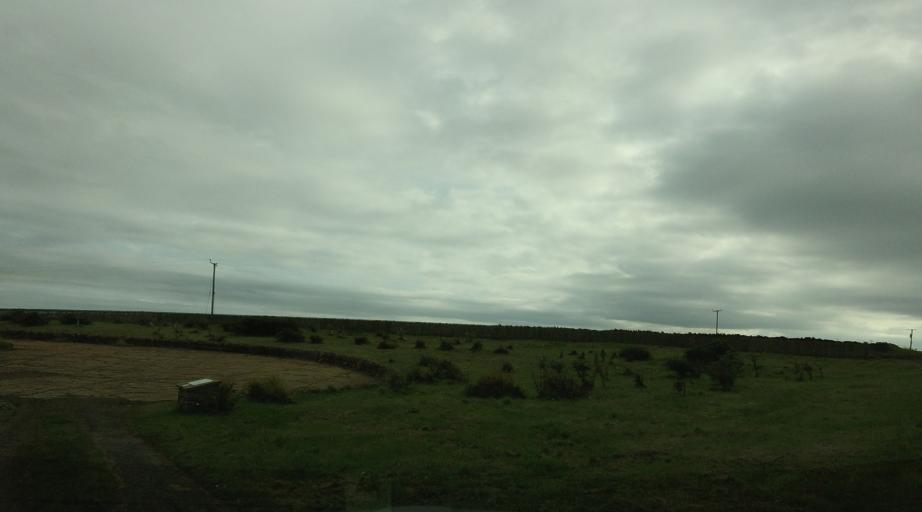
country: GB
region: Scotland
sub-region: Orkney Islands
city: Stromness
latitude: 59.0308
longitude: -3.3147
